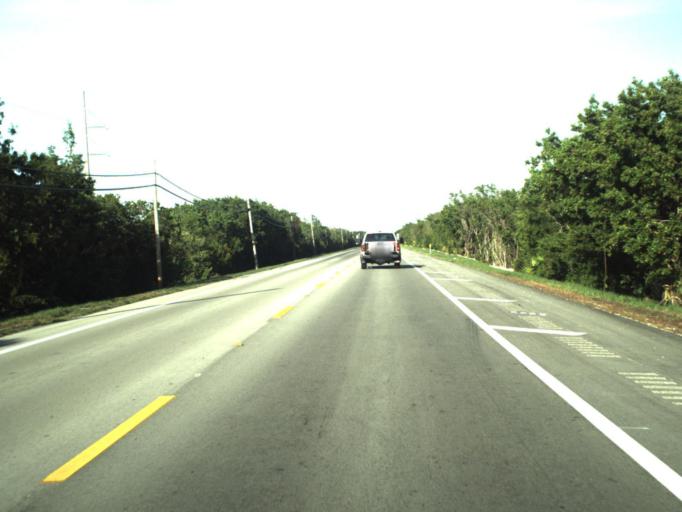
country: US
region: Florida
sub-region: Monroe County
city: Marathon
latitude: 24.7418
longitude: -80.9951
